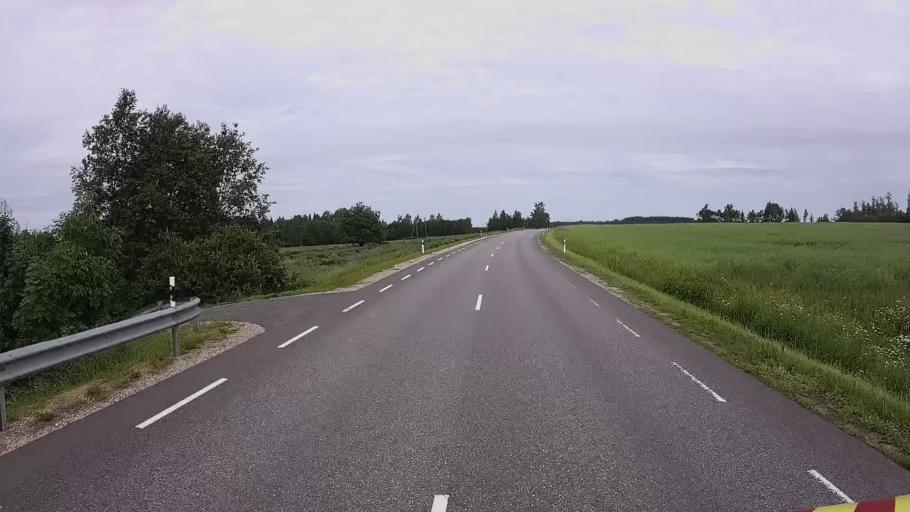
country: EE
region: Viljandimaa
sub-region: Karksi vald
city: Karksi-Nuia
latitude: 58.1610
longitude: 25.5893
